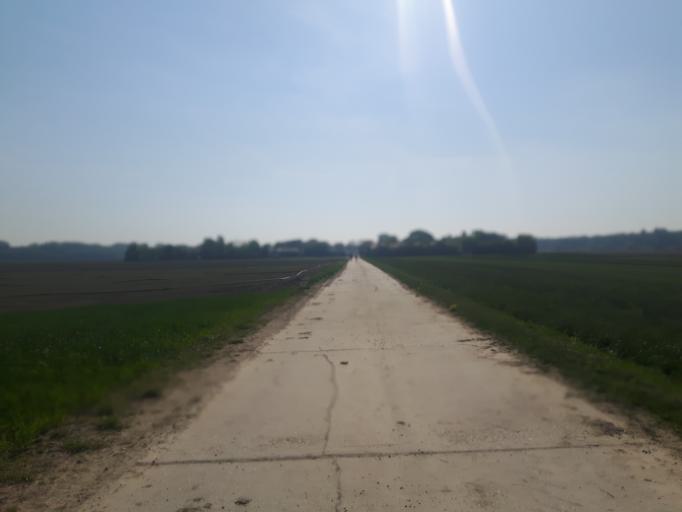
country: DE
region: Rheinland-Pfalz
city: Waldsee
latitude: 49.4059
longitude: 8.4518
